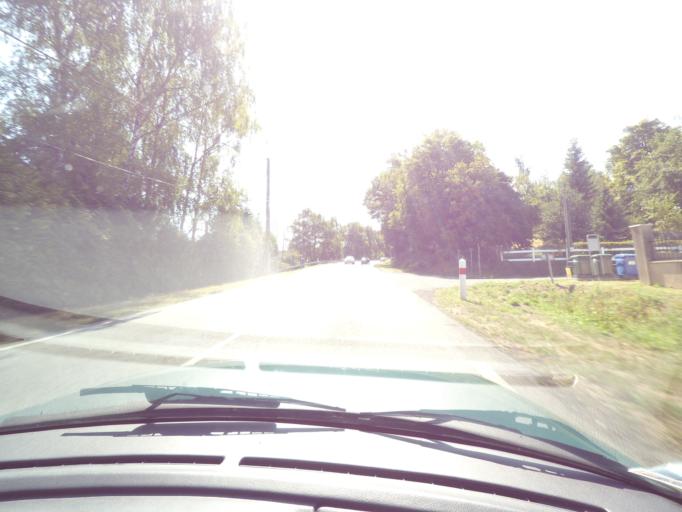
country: FR
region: Limousin
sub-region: Departement de la Haute-Vienne
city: Chaptelat
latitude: 45.9130
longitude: 1.2172
